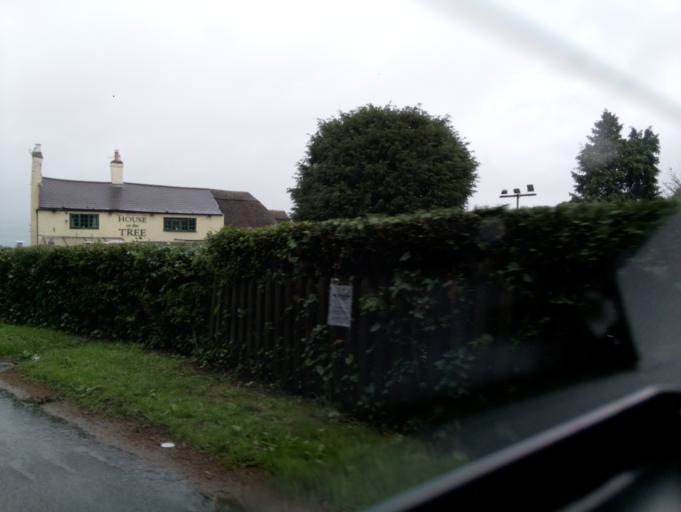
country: GB
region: England
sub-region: Gloucestershire
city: Uckington
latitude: 51.9128
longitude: -2.1433
